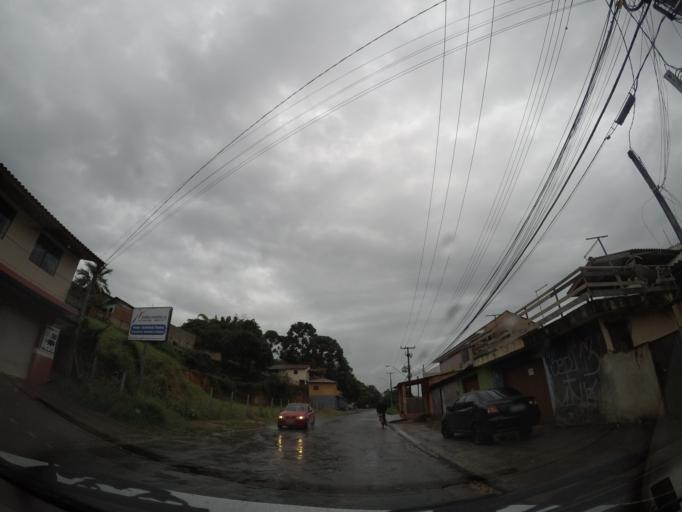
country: BR
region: Parana
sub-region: Curitiba
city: Curitiba
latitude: -25.4602
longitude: -49.3905
